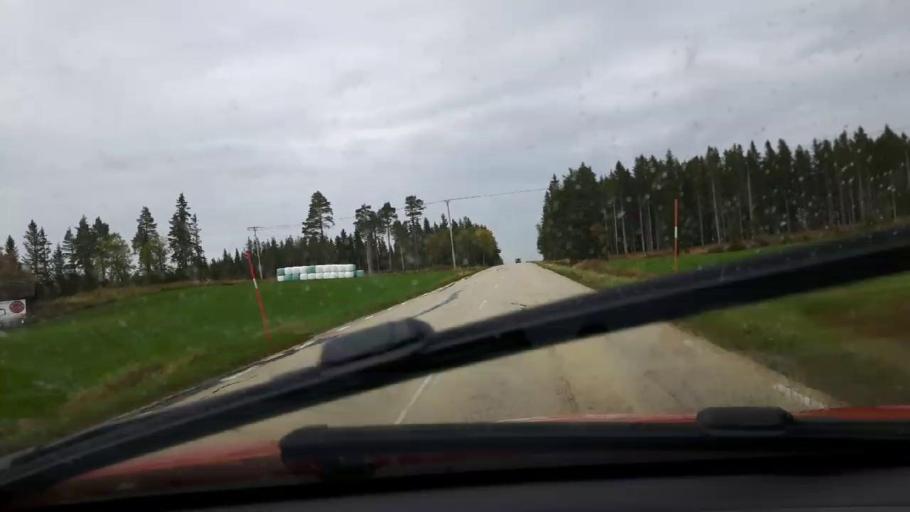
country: SE
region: Jaemtland
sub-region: Bergs Kommun
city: Hoverberg
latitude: 62.9404
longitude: 14.3347
